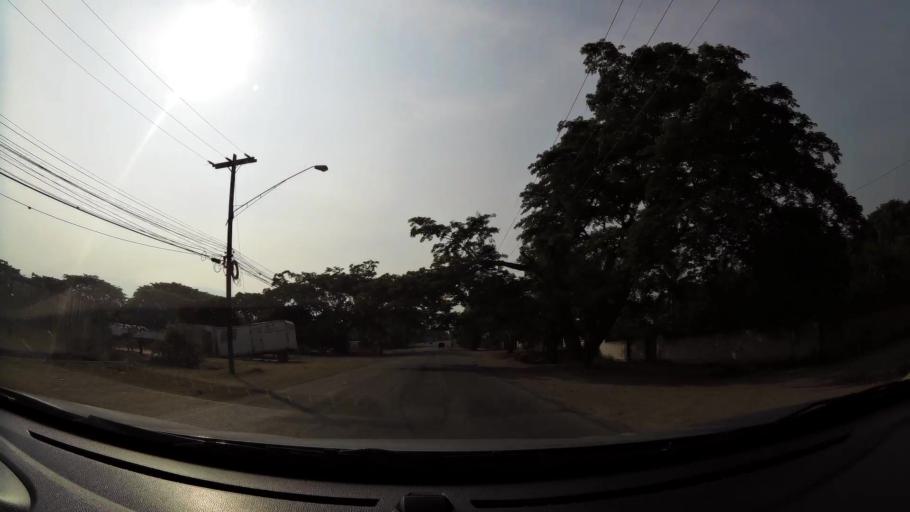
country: HN
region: Comayagua
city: Comayagua
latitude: 14.4524
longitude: -87.6479
